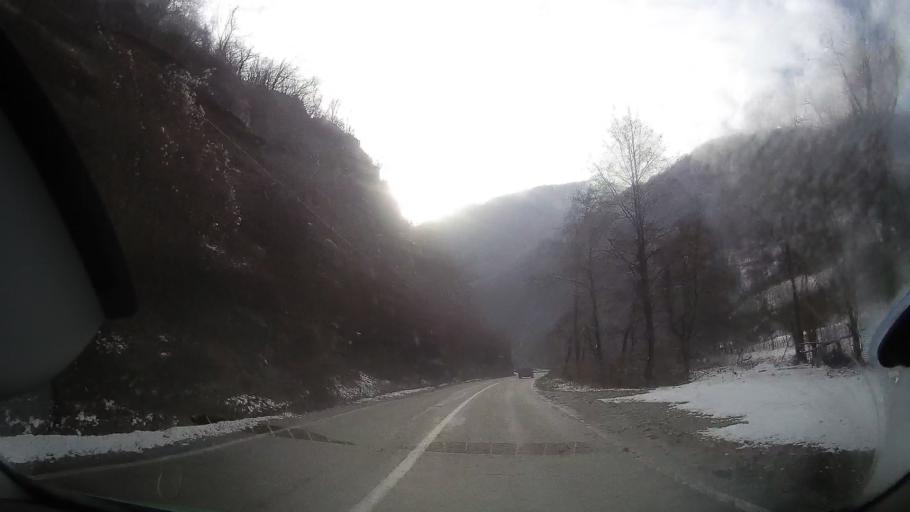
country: RO
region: Alba
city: Salciua de Sus
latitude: 46.4037
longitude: 23.3638
